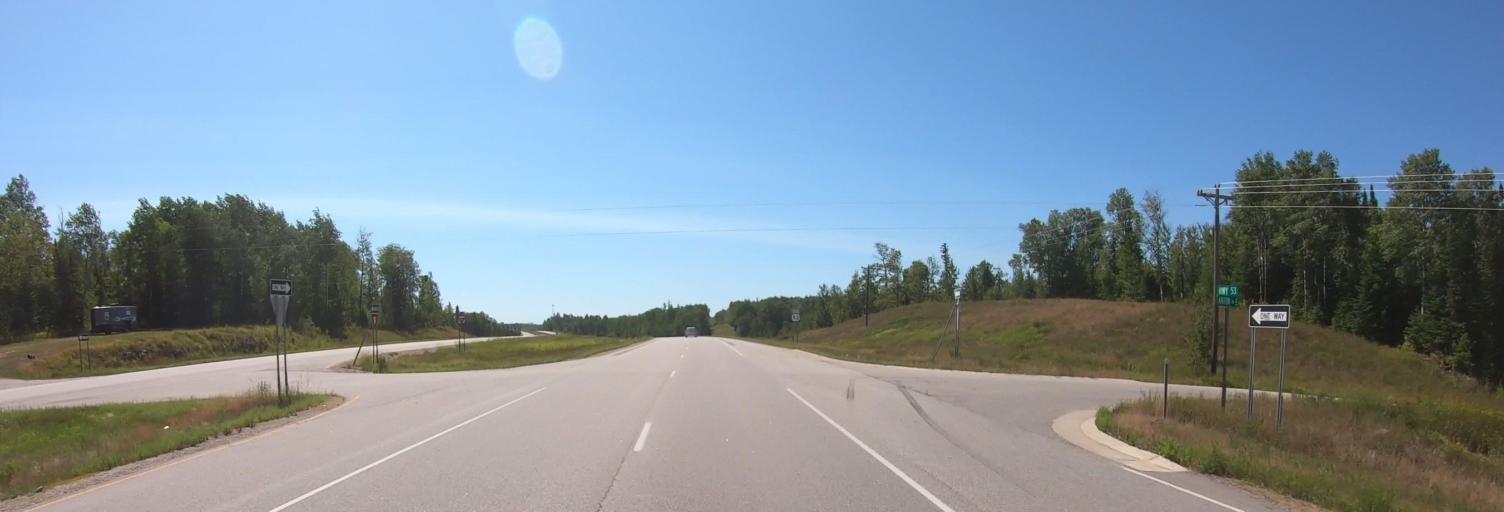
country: US
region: Minnesota
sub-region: Saint Louis County
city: Mountain Iron
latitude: 47.7583
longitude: -92.6550
